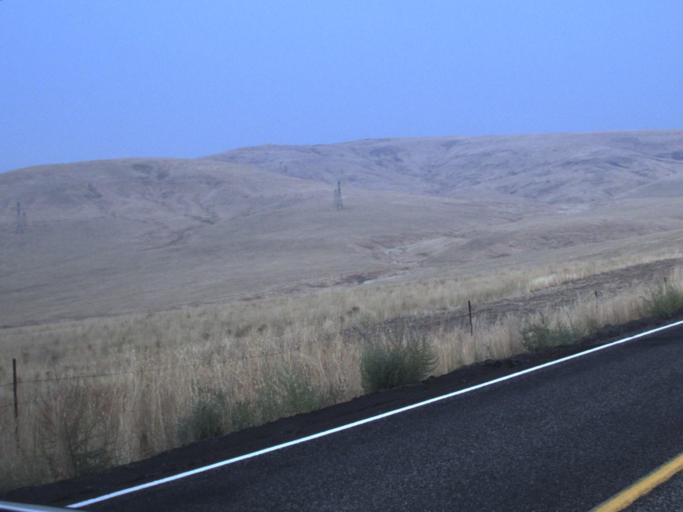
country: US
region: Washington
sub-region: Yakima County
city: Sunnyside
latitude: 46.4528
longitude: -119.9373
